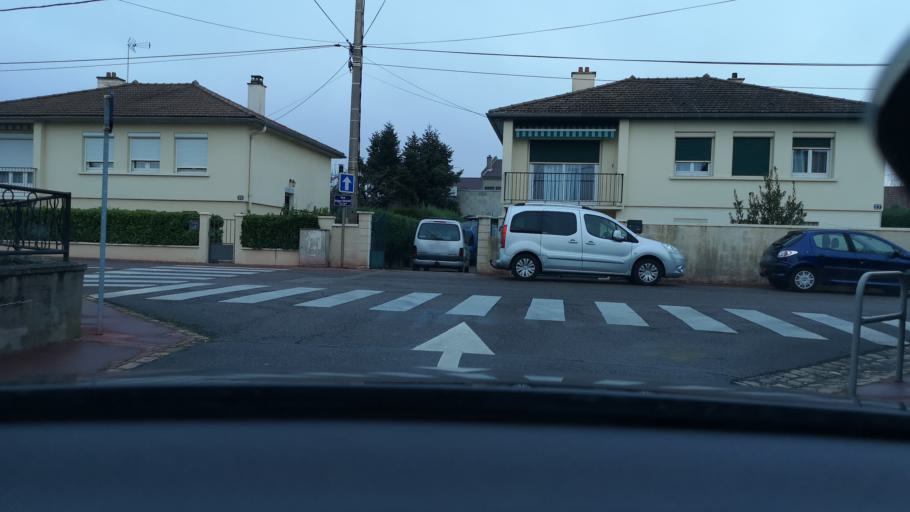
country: FR
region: Bourgogne
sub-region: Departement de Saone-et-Loire
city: Champforgeuil
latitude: 46.8049
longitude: 4.8468
